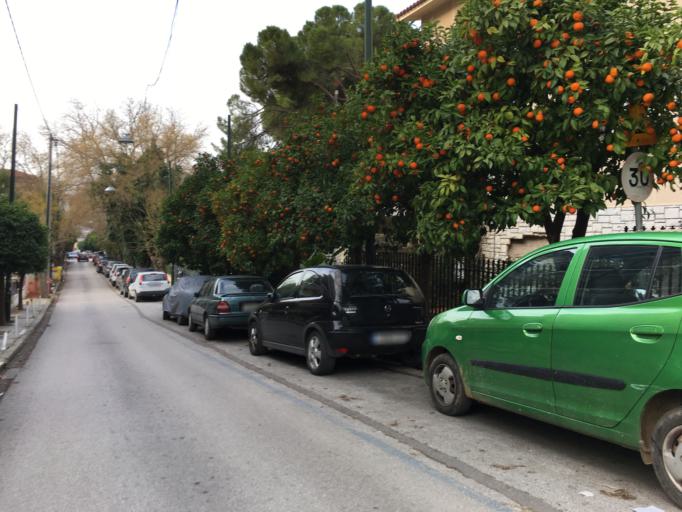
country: GR
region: Attica
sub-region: Nomarchia Athinas
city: Khalandrion
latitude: 38.0237
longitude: 23.8027
